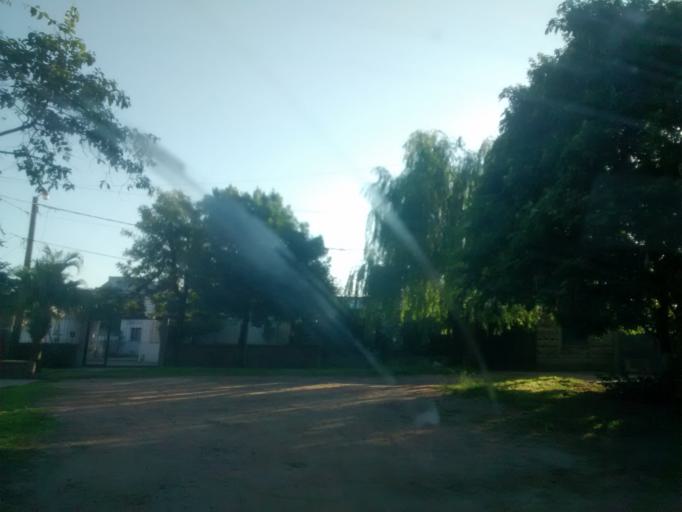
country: AR
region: Chaco
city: Resistencia
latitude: -27.4704
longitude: -58.9821
